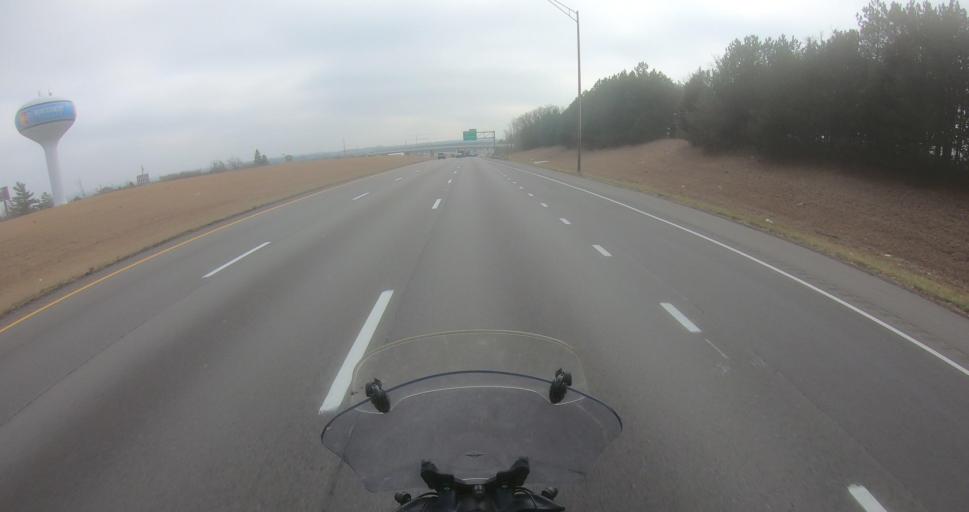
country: US
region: Ohio
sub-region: Montgomery County
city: West Carrollton City
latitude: 39.6332
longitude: -84.2309
